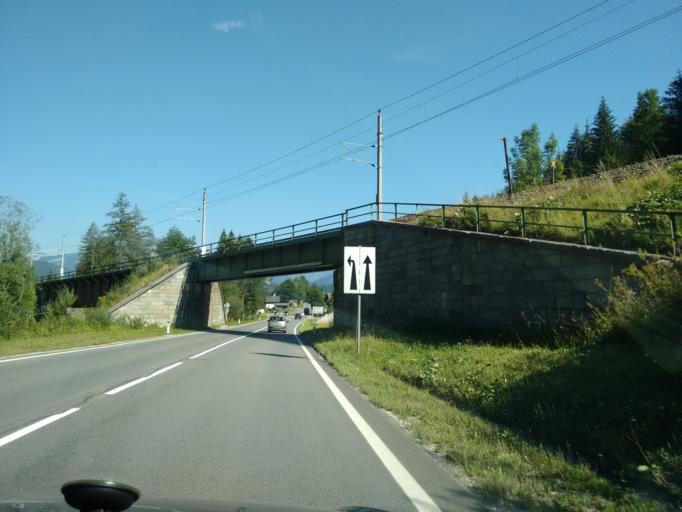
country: AT
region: Styria
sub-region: Politischer Bezirk Liezen
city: Bad Aussee
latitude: 47.5919
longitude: 13.7950
